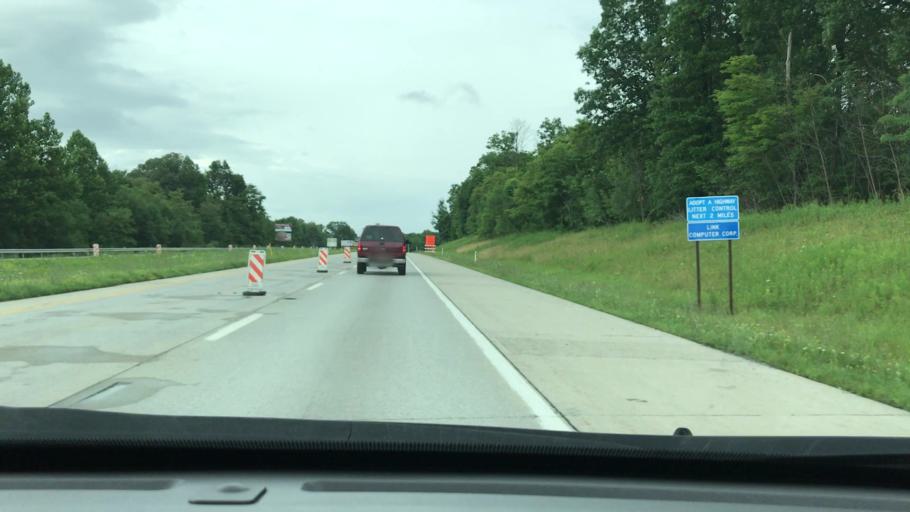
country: US
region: Pennsylvania
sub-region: Blair County
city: Bellwood
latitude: 40.6100
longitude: -78.3081
